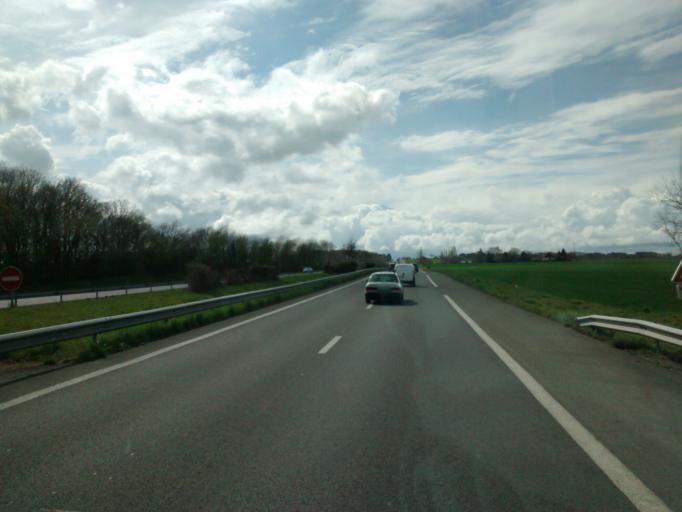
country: FR
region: Brittany
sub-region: Departement d'Ille-et-Vilaine
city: Breal-sous-Montfort
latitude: 48.0574
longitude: -1.8975
